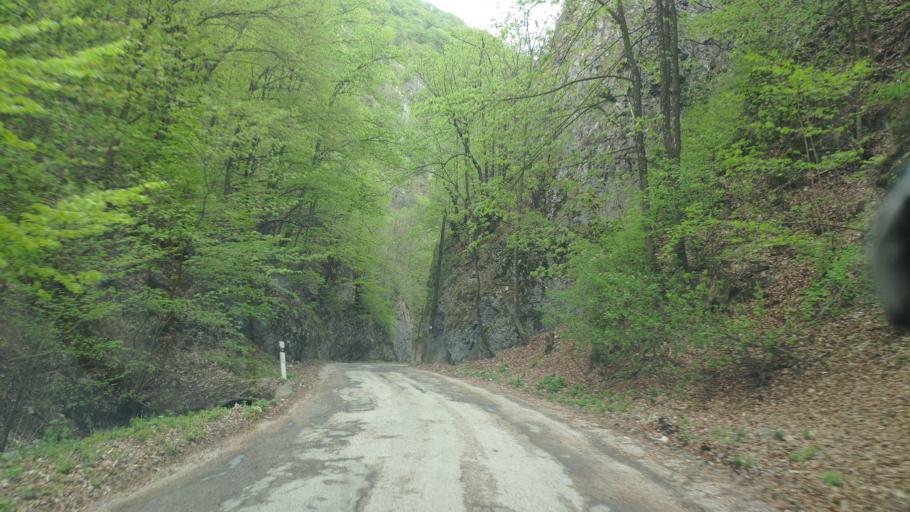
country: SK
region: Kosicky
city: Medzev
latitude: 48.6521
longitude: 20.8465
